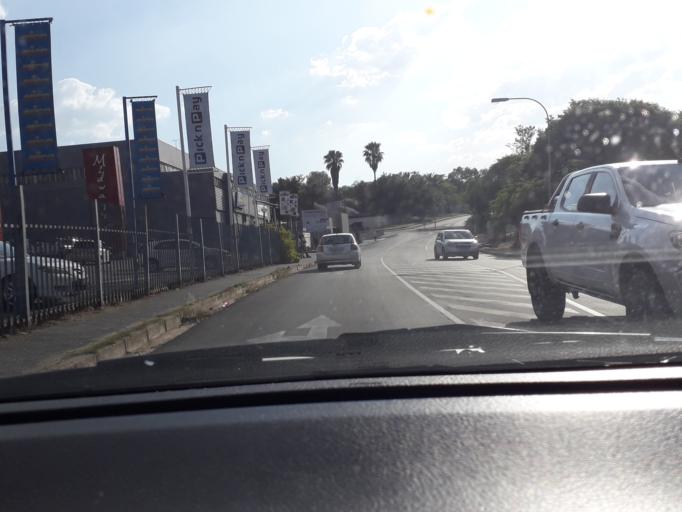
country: ZA
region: Gauteng
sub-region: City of Johannesburg Metropolitan Municipality
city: Modderfontein
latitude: -26.1254
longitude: 28.0935
